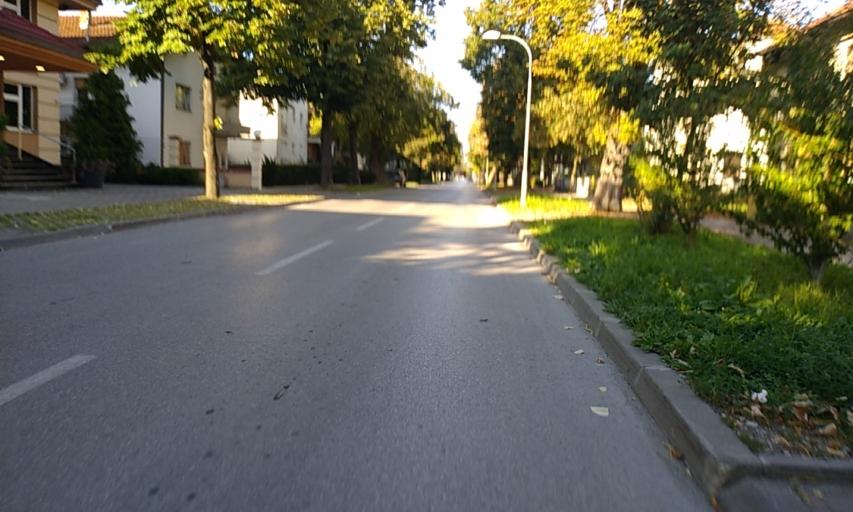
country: BA
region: Republika Srpska
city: Banja Luka
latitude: 44.7780
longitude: 17.1900
